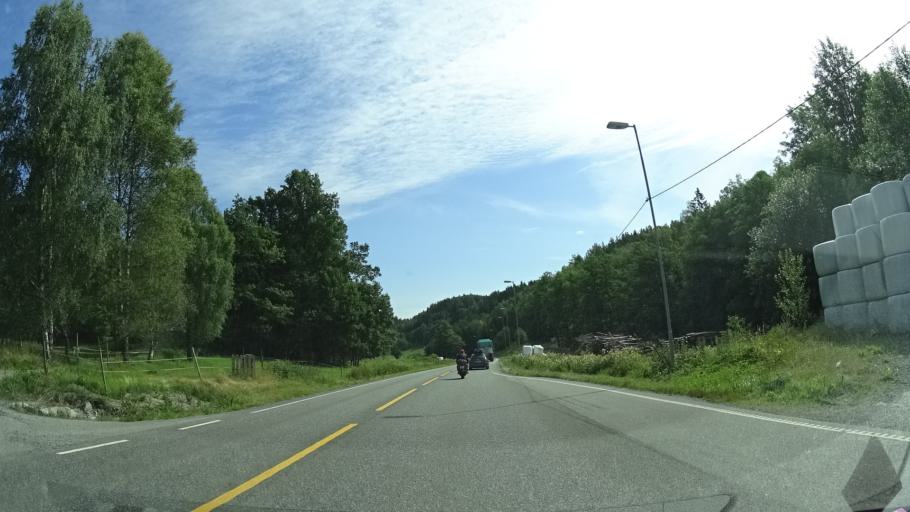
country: NO
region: Telemark
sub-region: Bamble
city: Langesund
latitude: 58.9849
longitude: 9.6197
